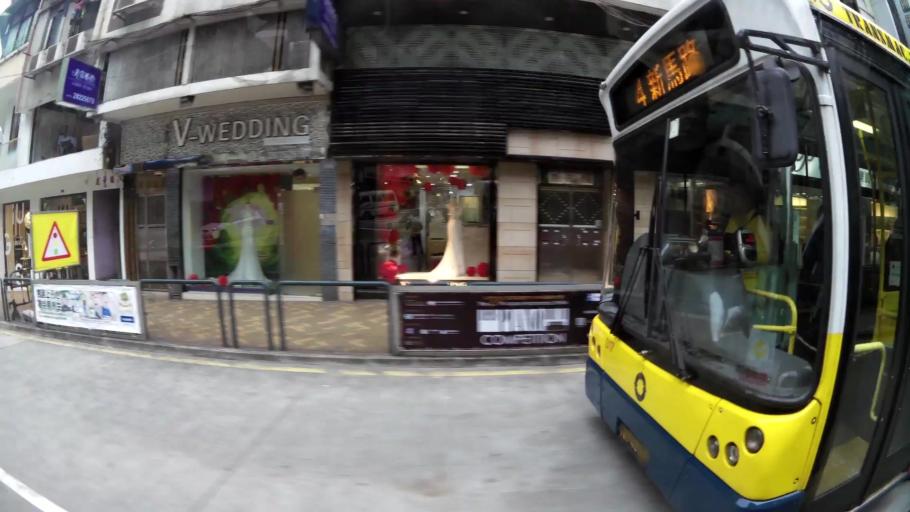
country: MO
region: Macau
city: Macau
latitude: 22.1962
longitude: 113.5460
